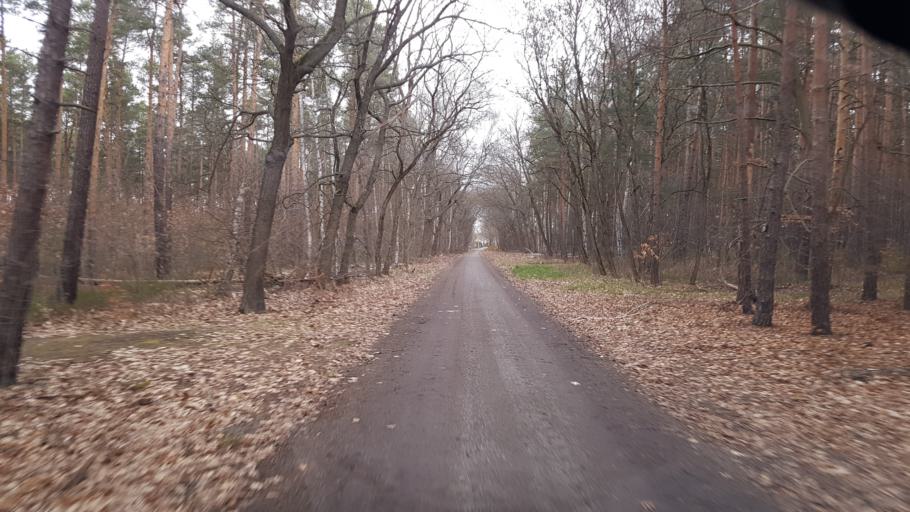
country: DE
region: Brandenburg
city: Finsterwalde
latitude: 51.5798
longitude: 13.7001
